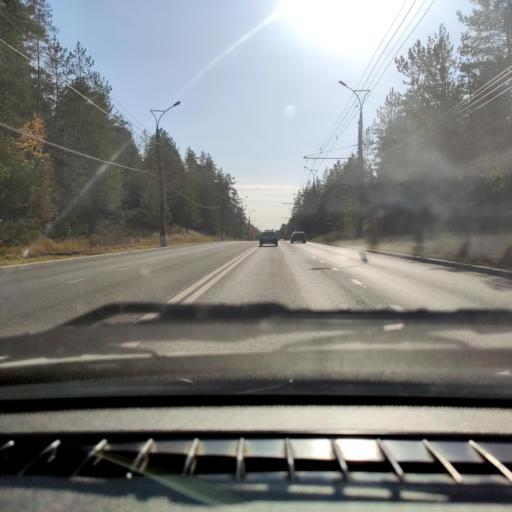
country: RU
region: Samara
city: Zhigulevsk
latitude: 53.4949
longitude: 49.4630
